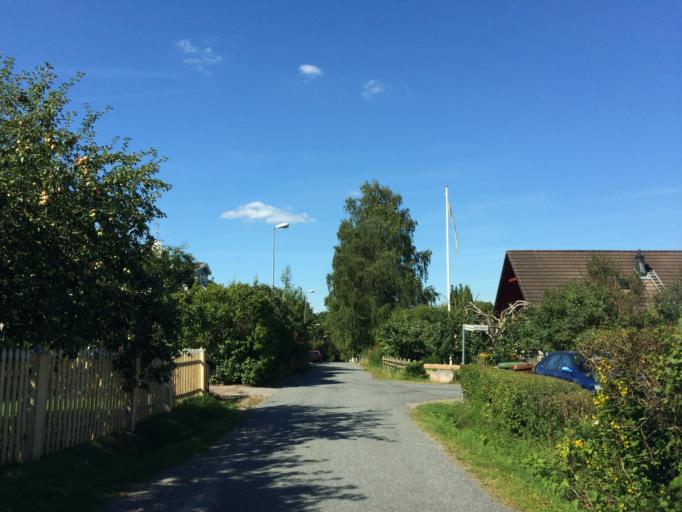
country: SE
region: Stockholm
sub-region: Sollentuna Kommun
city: Sollentuna
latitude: 59.4539
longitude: 17.9115
